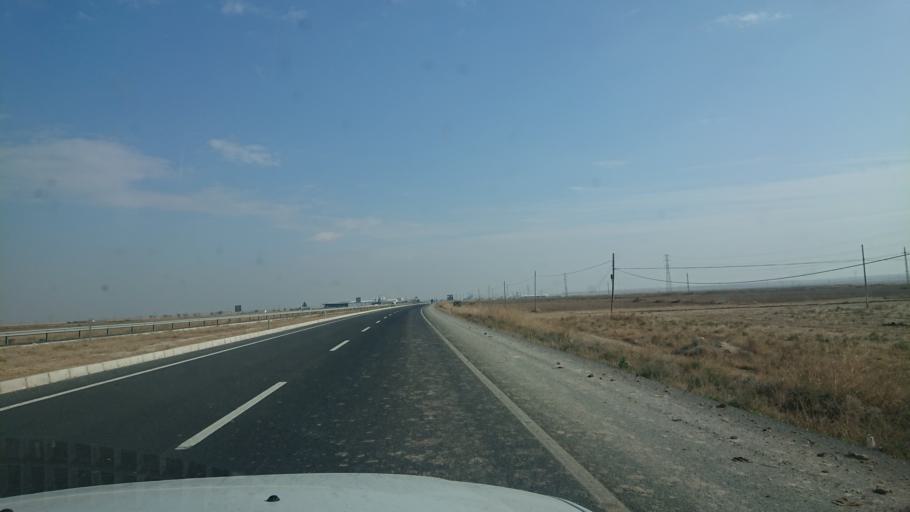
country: TR
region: Aksaray
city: Yesilova
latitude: 38.3108
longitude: 33.8331
